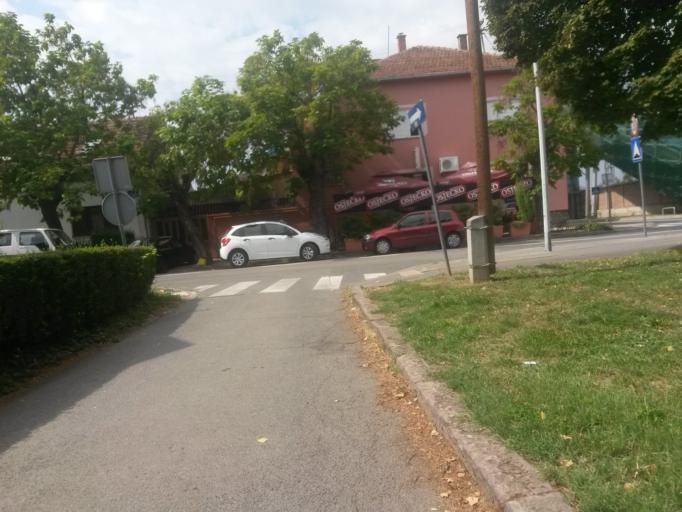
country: HR
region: Osjecko-Baranjska
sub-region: Grad Osijek
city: Osijek
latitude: 45.5519
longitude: 18.6835
